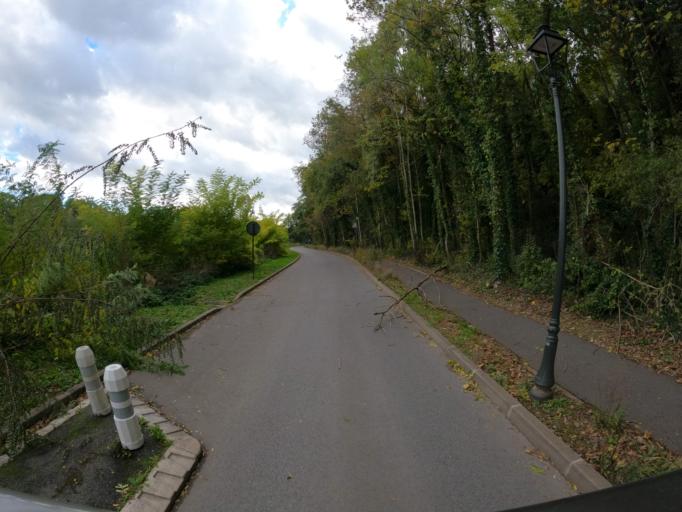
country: FR
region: Ile-de-France
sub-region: Departement de Seine-et-Marne
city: Coupvray
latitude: 48.9016
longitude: 2.7978
